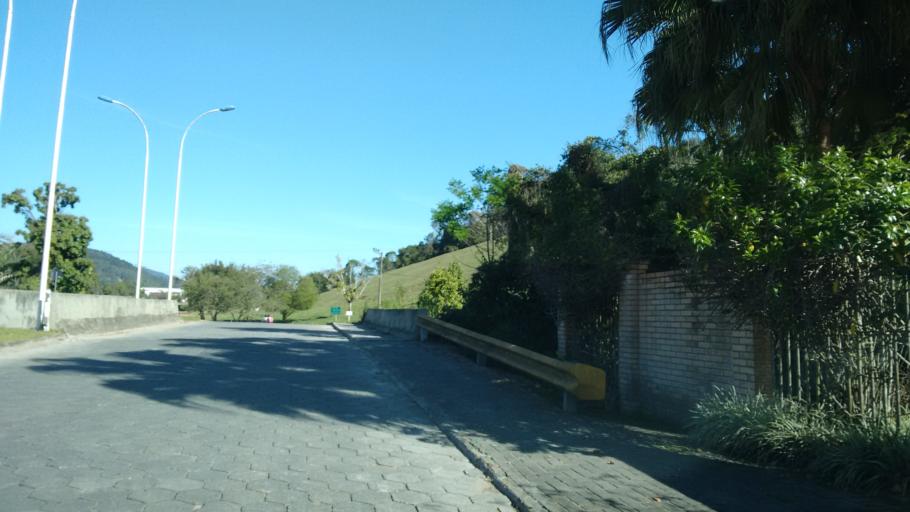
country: BR
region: Santa Catarina
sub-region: Pomerode
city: Pomerode
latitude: -26.7614
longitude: -49.1724
